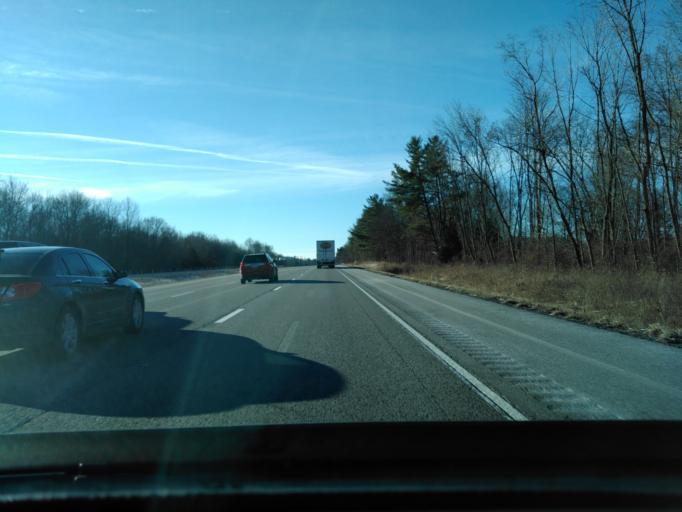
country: US
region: Illinois
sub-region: Williamson County
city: Johnston City
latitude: 37.7863
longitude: -88.9460
